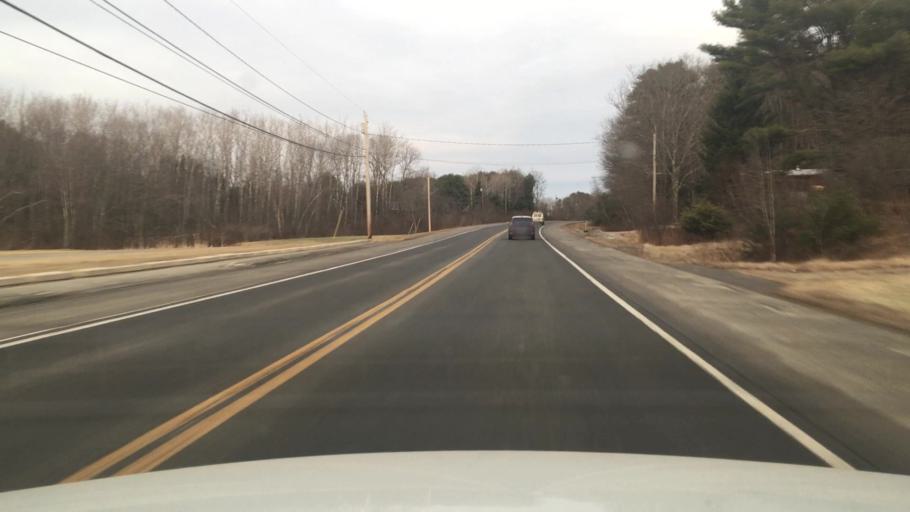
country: US
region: Maine
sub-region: Lincoln County
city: Damariscotta
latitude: 44.0191
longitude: -69.5803
